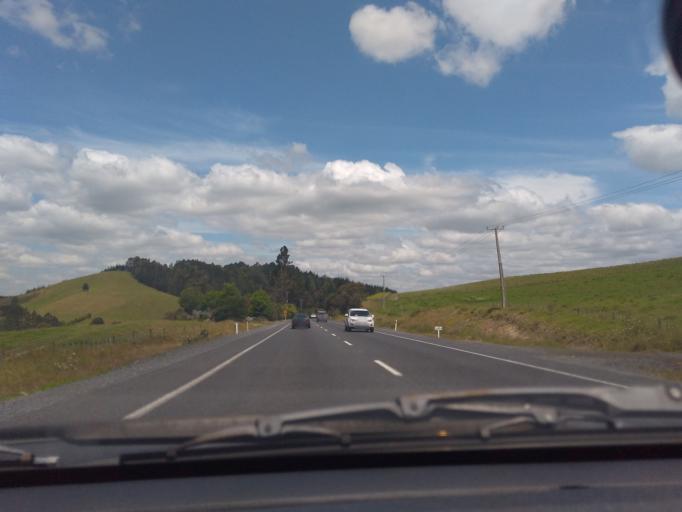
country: NZ
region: Northland
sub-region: Far North District
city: Kerikeri
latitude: -35.2796
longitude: 173.9539
